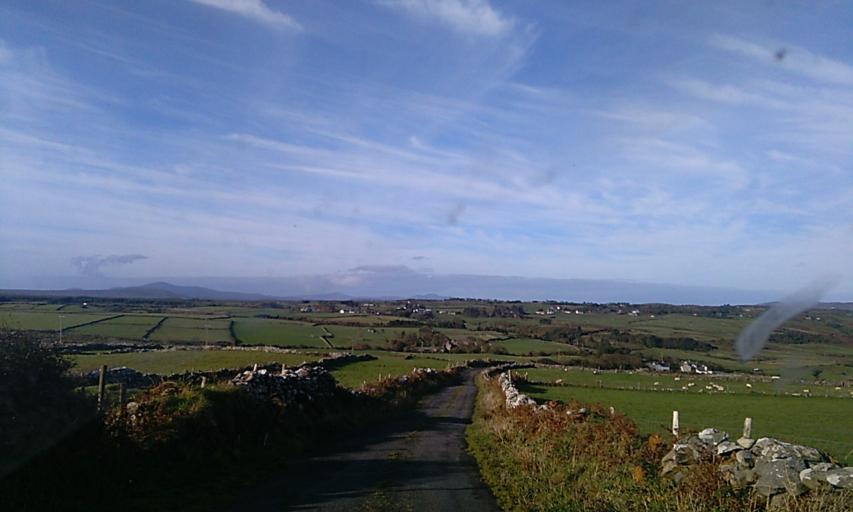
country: IE
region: Ulster
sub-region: County Donegal
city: Moville
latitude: 55.2680
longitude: -7.0579
